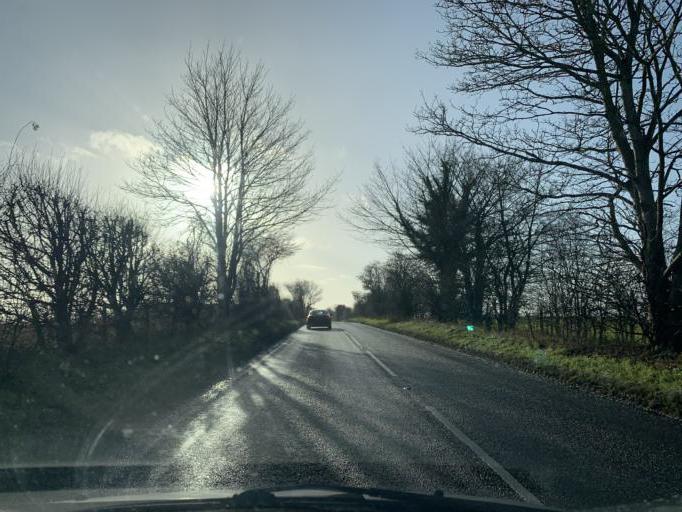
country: GB
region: England
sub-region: Wiltshire
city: Winterbourne Stoke
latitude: 51.1576
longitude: -1.8591
